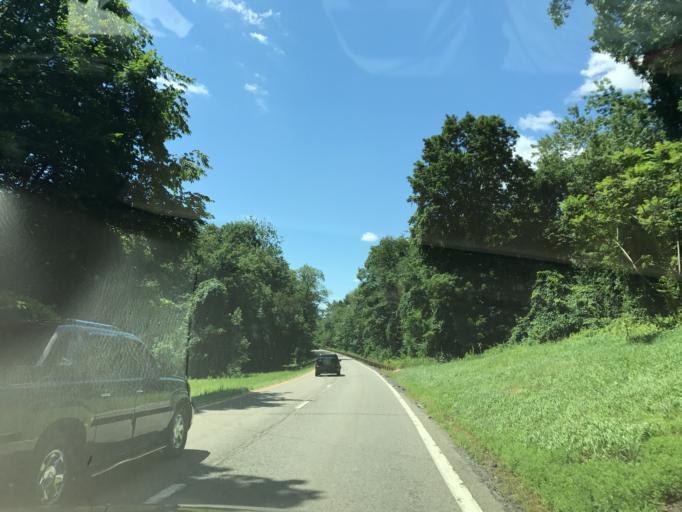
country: US
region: New York
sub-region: Dutchess County
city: Hillside Lake
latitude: 41.5672
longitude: -73.7821
